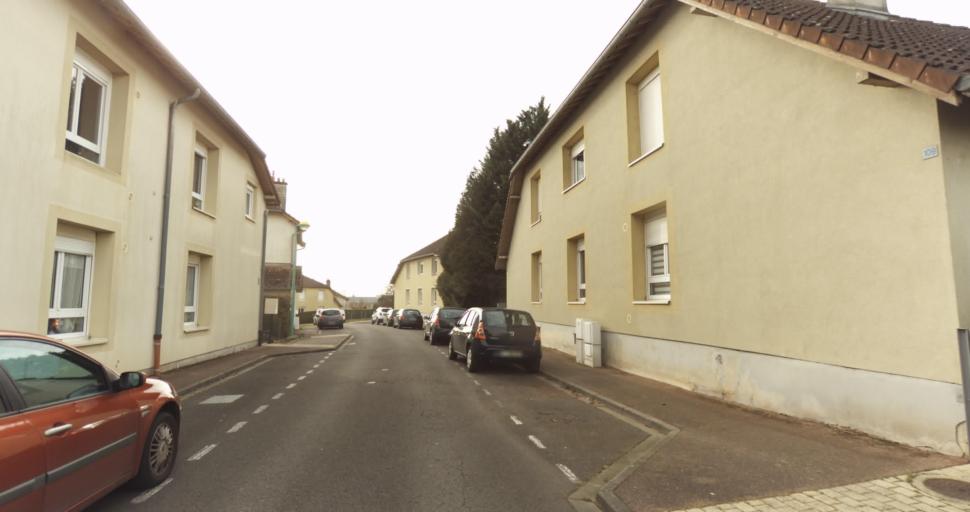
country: FR
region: Lorraine
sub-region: Departement de Meurthe-et-Moselle
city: Jarny
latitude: 49.1626
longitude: 5.8786
